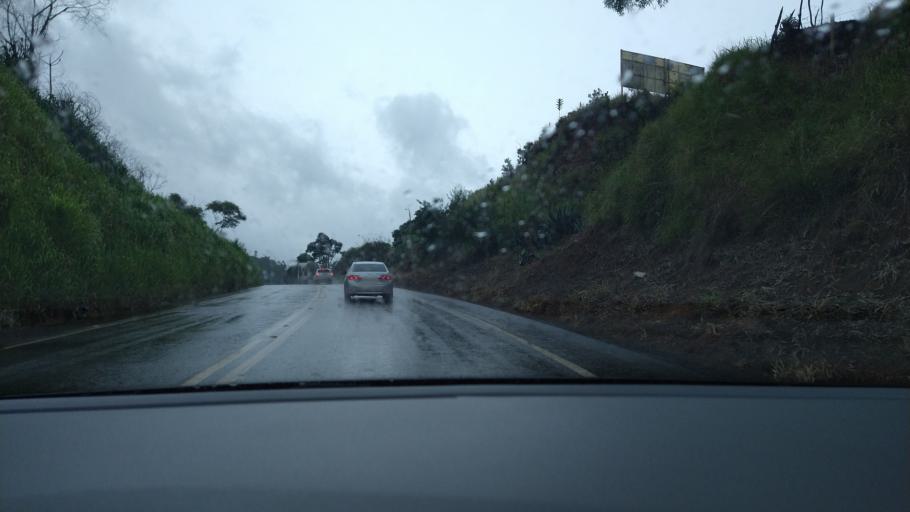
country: BR
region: Minas Gerais
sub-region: Vicosa
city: Vicosa
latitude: -20.6174
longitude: -42.8674
